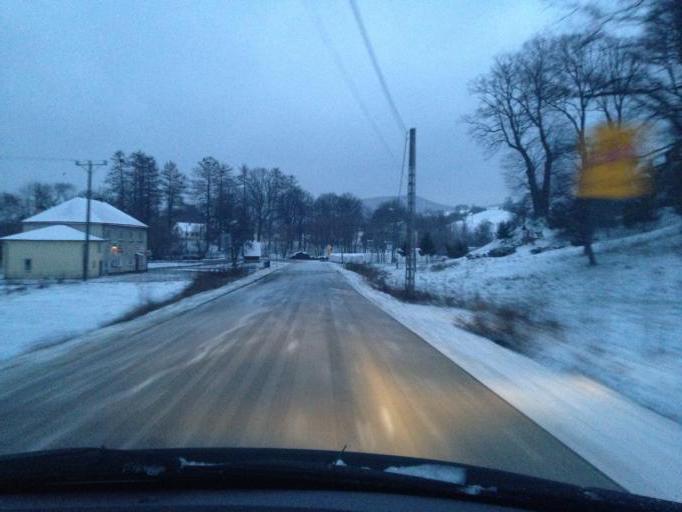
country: PL
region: Subcarpathian Voivodeship
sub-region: Powiat jasielski
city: Krempna
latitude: 49.5275
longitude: 21.5549
